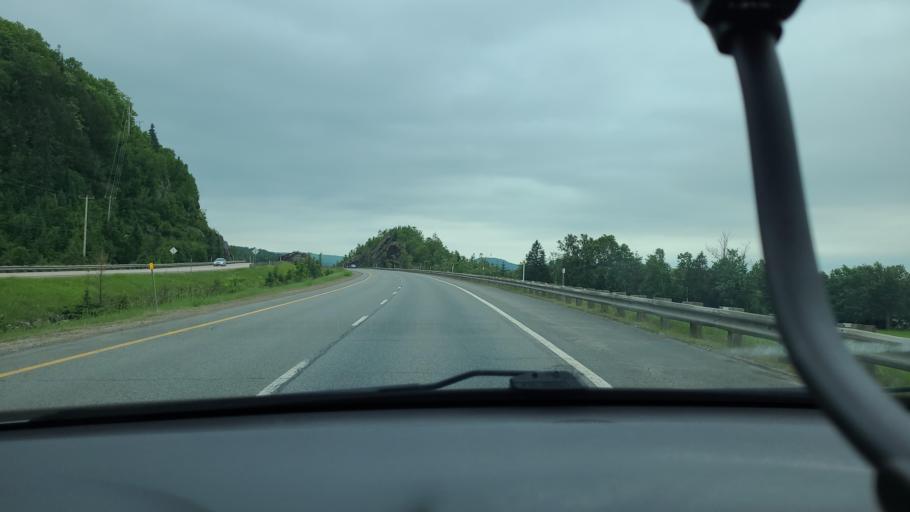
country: CA
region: Quebec
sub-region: Laurentides
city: Labelle
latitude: 46.1634
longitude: -74.7088
